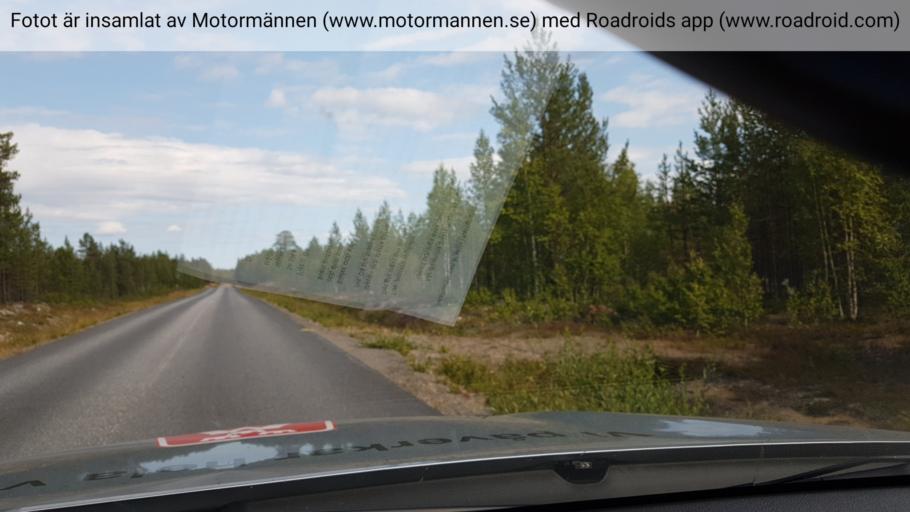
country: SE
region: Vaesterbotten
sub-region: Skelleftea Kommun
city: Boliden
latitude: 65.3161
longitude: 20.2853
